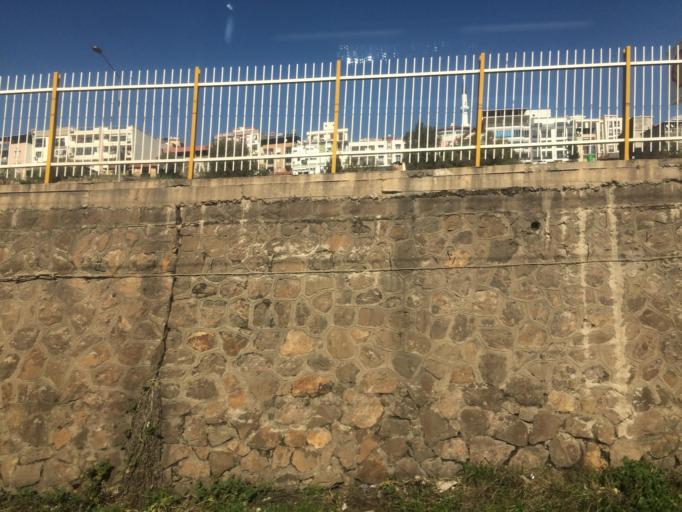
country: TR
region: Izmir
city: Karsiyaka
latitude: 38.4651
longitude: 27.1359
